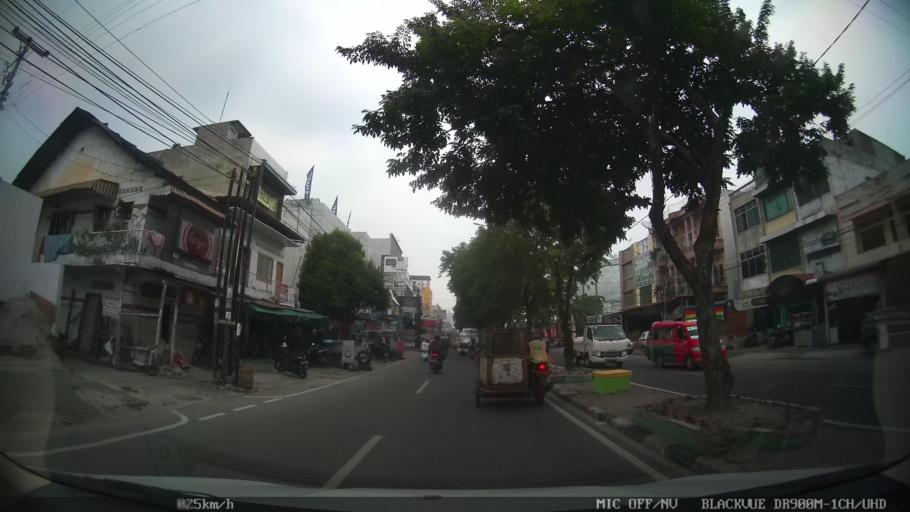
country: ID
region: North Sumatra
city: Medan
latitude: 3.5757
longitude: 98.7035
